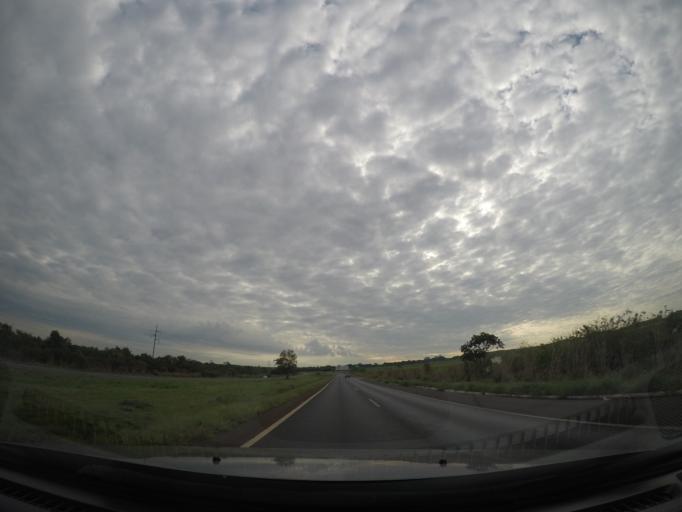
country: BR
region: Goias
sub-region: Planaltina
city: Planaltina
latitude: -15.5985
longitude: -47.6205
